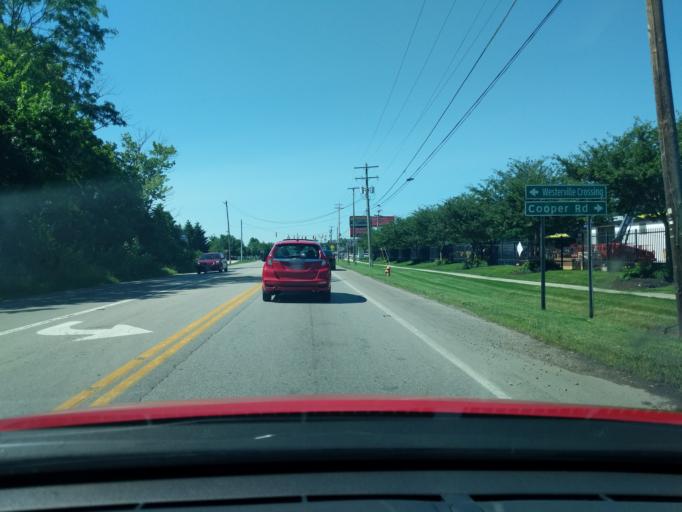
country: US
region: Ohio
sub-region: Franklin County
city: Huber Ridge
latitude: 40.0895
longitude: -82.9263
